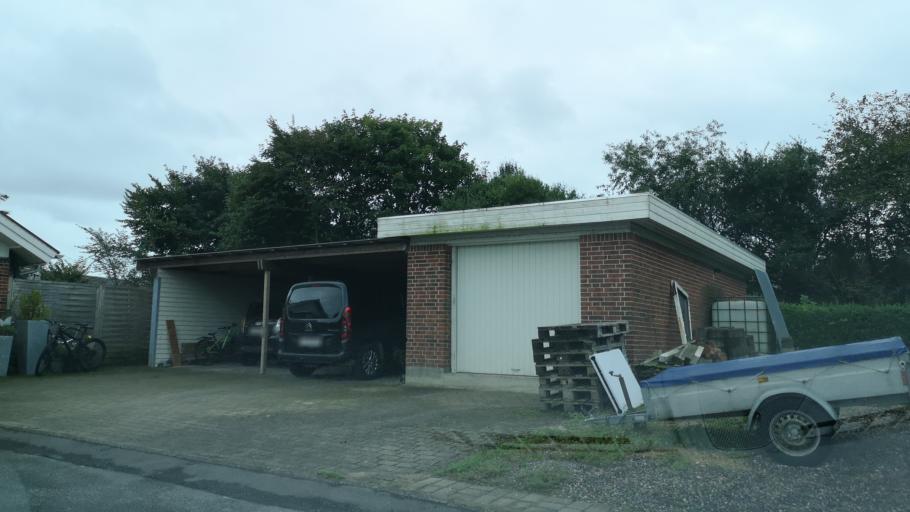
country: DK
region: Central Jutland
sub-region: Ringkobing-Skjern Kommune
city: Videbaek
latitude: 56.0861
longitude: 8.6982
